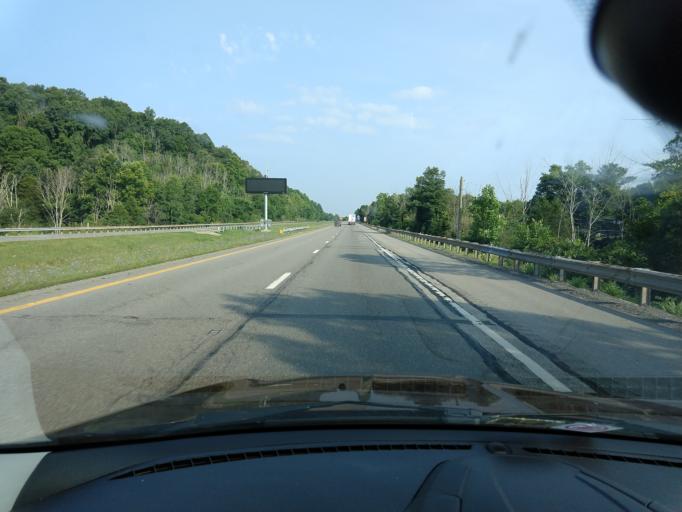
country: US
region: West Virginia
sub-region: Jackson County
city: Ripley
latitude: 38.7370
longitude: -81.6675
